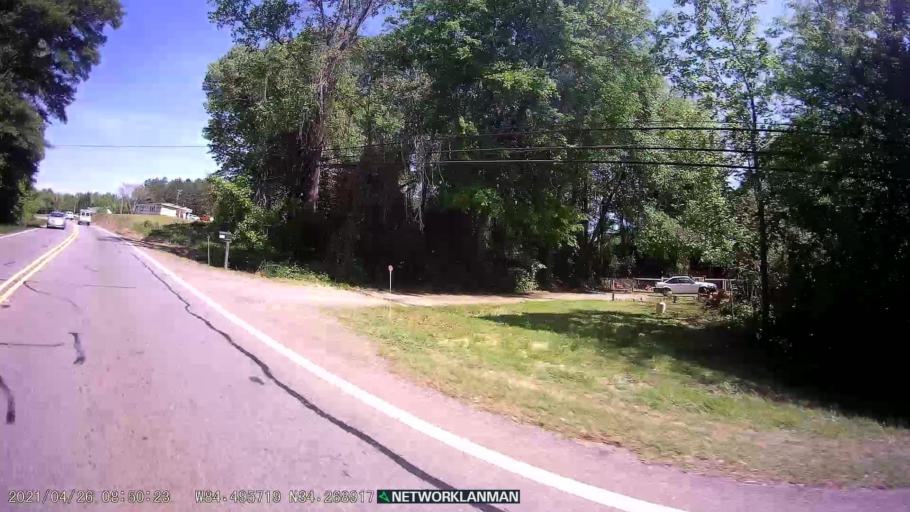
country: US
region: Georgia
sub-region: Cherokee County
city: Canton
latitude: 34.2682
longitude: -84.4972
